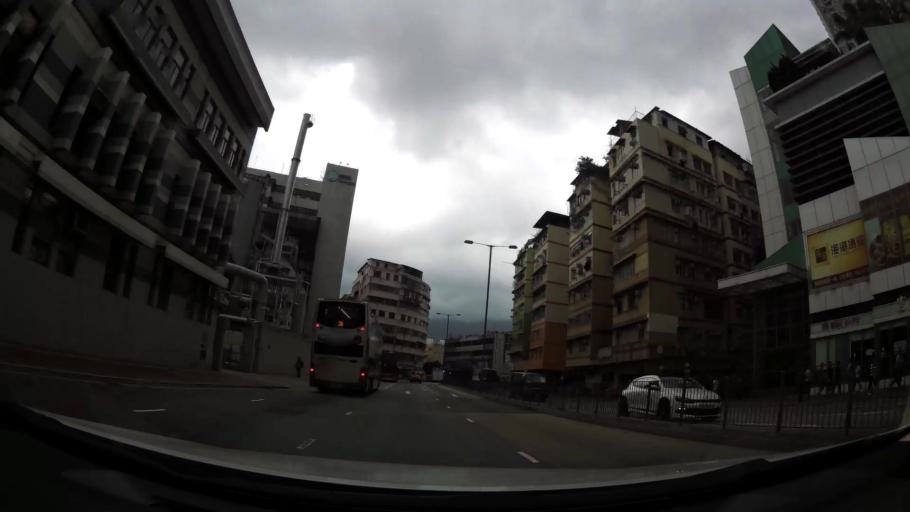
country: HK
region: Kowloon City
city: Kowloon
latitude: 22.3199
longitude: 114.1929
